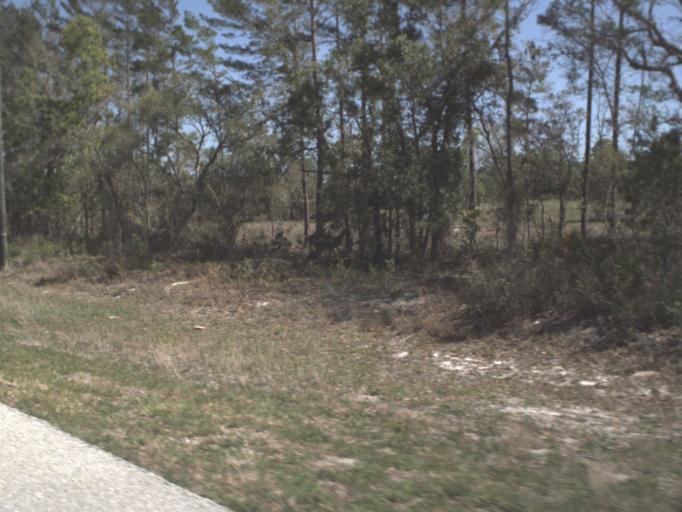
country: US
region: Florida
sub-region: Flagler County
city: Palm Coast
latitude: 29.6433
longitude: -81.2858
